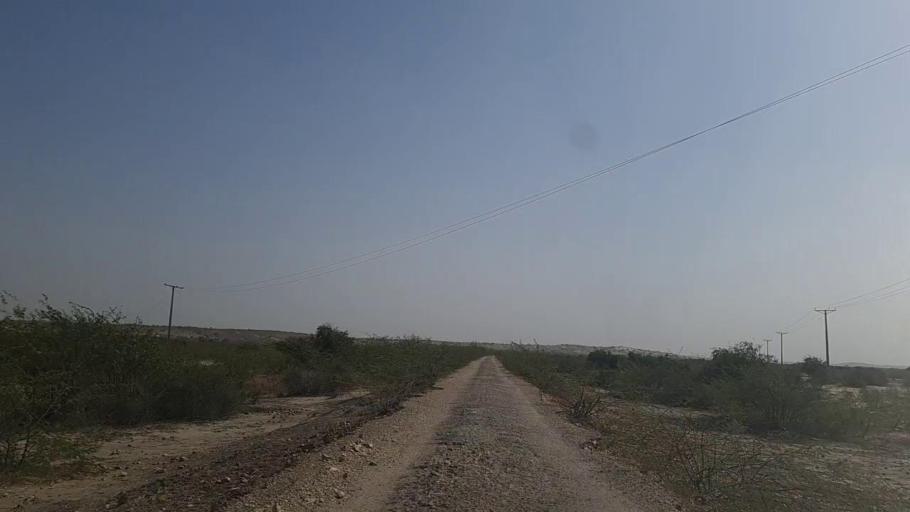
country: PK
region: Sindh
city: Naukot
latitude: 24.5866
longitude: 69.2927
